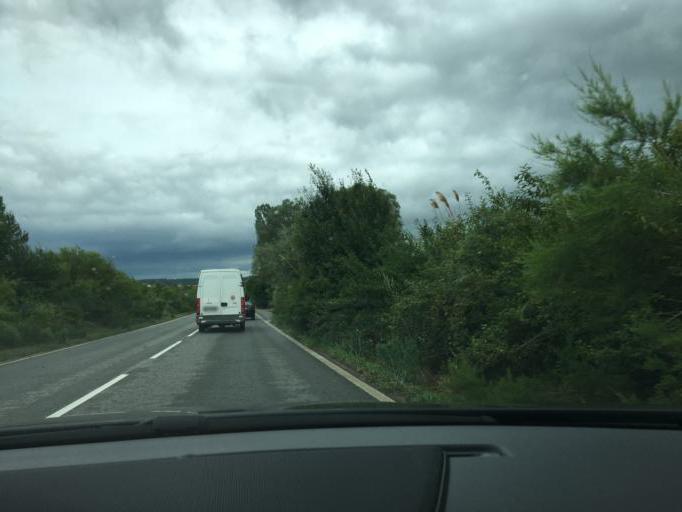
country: BG
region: Kyustendil
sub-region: Obshtina Bobovdol
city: Bobovdol
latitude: 42.2743
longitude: 23.0041
